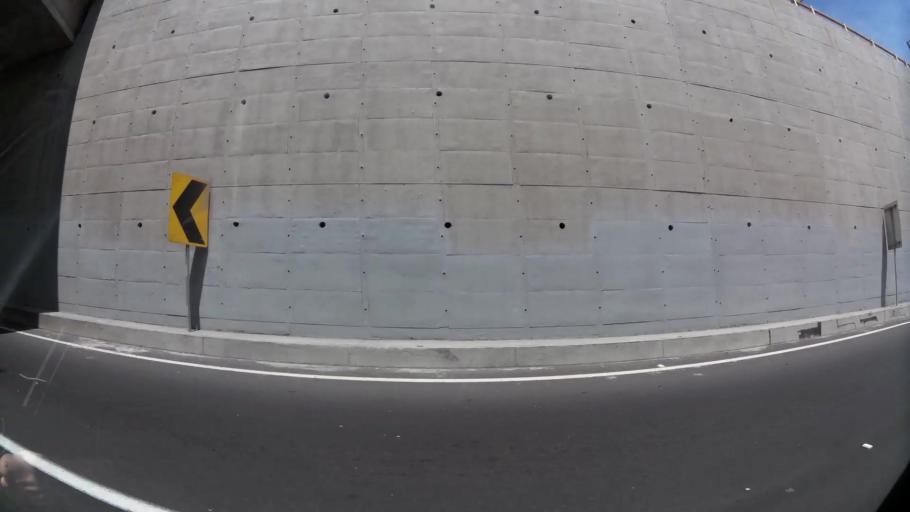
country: EC
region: Pichincha
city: Sangolqui
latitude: -0.2250
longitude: -78.3481
